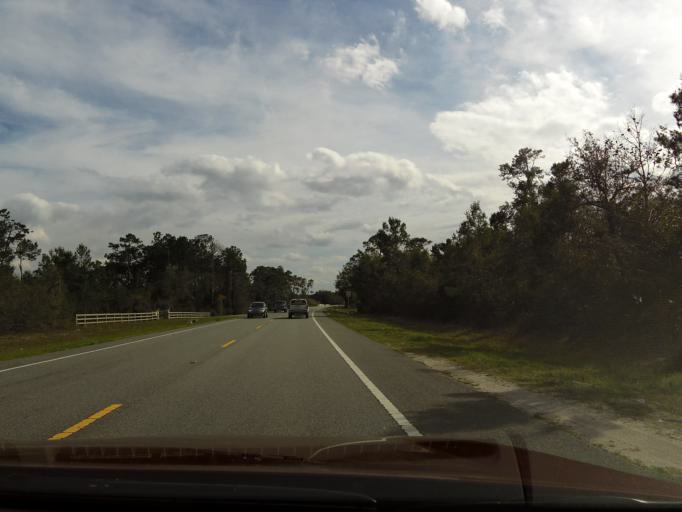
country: US
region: Florida
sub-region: Volusia County
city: De Leon Springs
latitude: 29.1850
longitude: -81.3060
